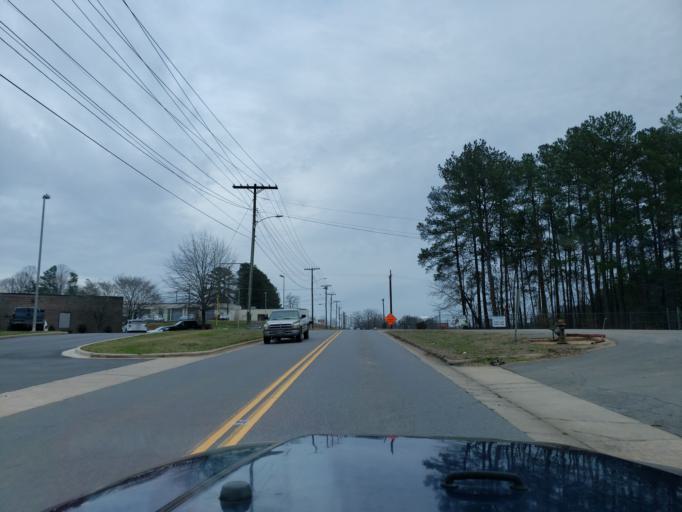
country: US
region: North Carolina
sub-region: Cleveland County
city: Shelby
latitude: 35.3044
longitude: -81.5614
